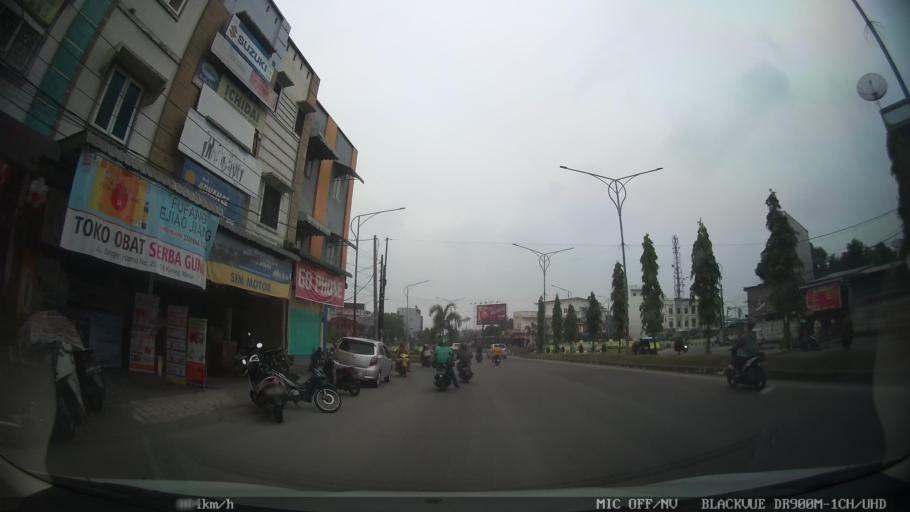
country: ID
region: North Sumatra
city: Deli Tua
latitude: 3.5377
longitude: 98.6846
